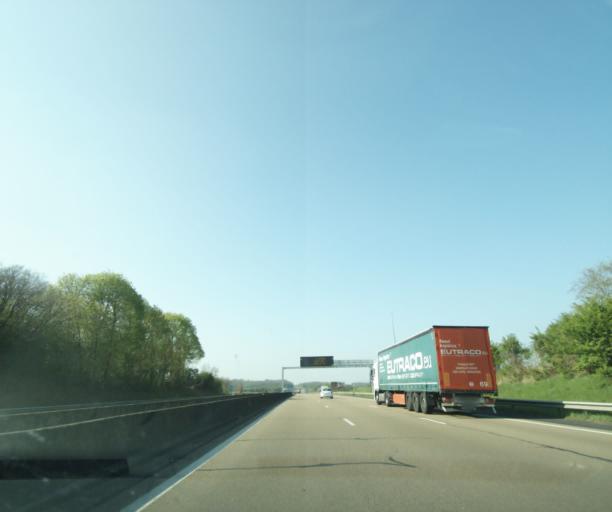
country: FR
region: Ile-de-France
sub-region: Departement de Seine-et-Marne
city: Cely
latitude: 48.4388
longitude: 2.5348
